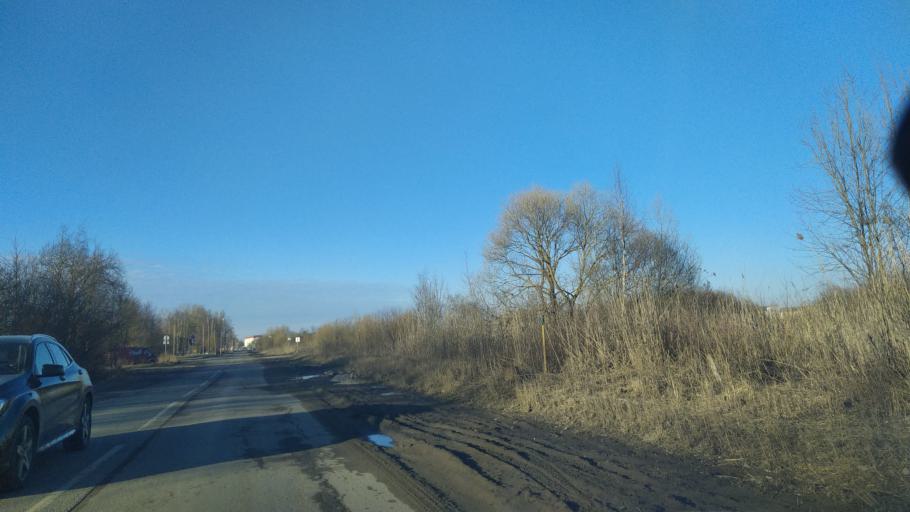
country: RU
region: St.-Petersburg
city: Pushkin
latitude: 59.6943
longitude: 30.3960
